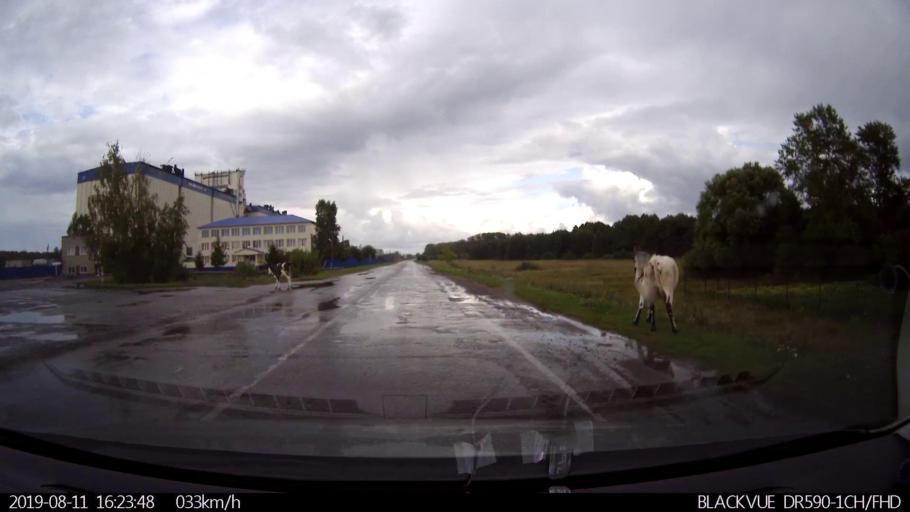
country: RU
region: Ulyanovsk
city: Mayna
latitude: 54.0972
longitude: 47.5894
